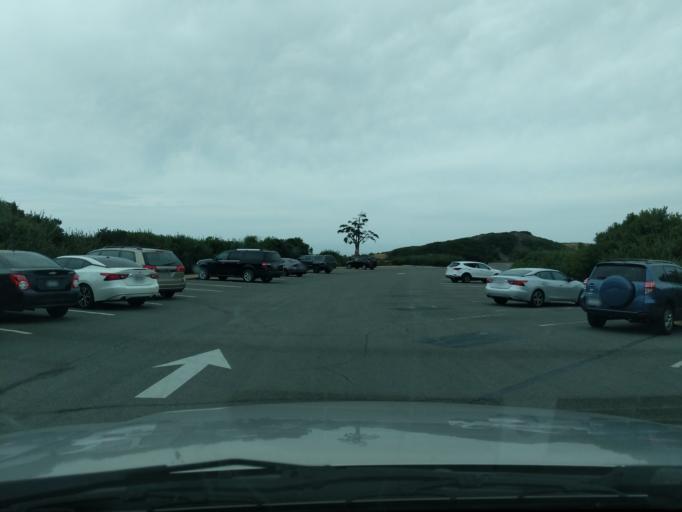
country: US
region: California
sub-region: San Diego County
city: Coronado
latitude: 32.6743
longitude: -117.2413
